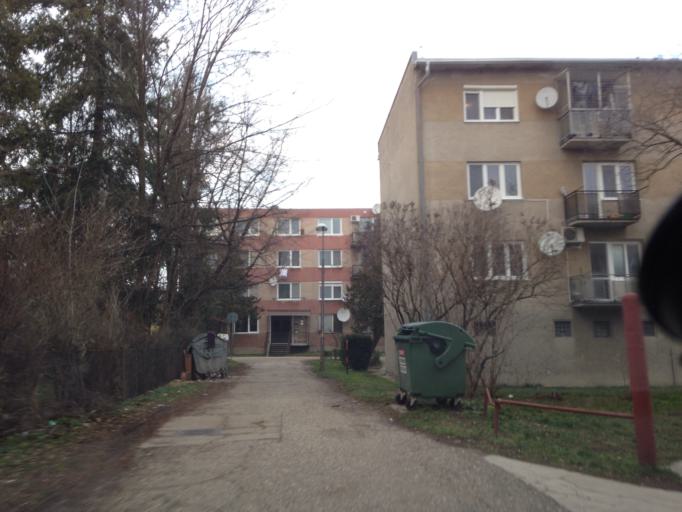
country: SK
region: Nitriansky
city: Komarno
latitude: 47.7614
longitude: 18.1365
